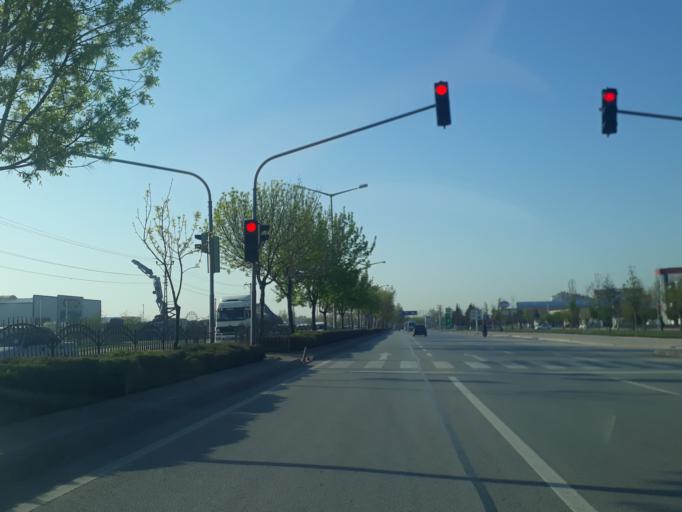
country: TR
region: Konya
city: Selcuklu
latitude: 37.8788
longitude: 32.5462
